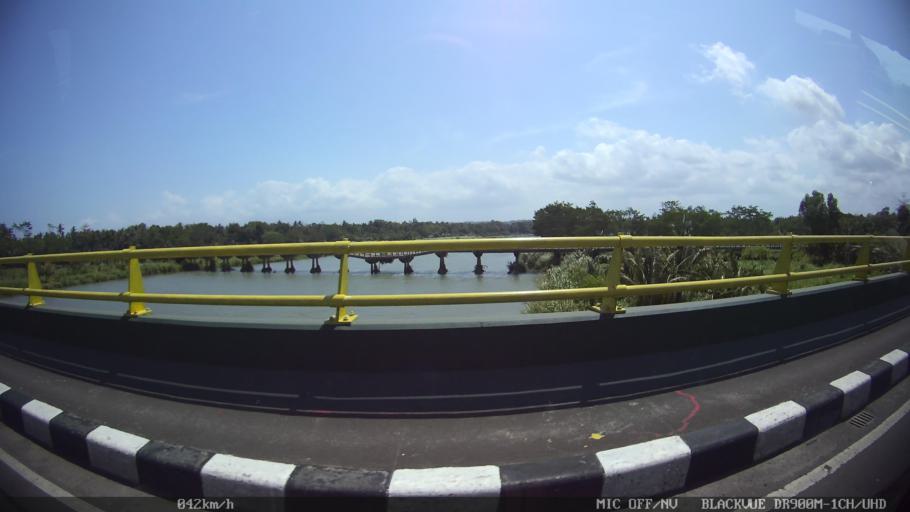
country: ID
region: Daerah Istimewa Yogyakarta
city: Srandakan
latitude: -7.9392
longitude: 110.2435
